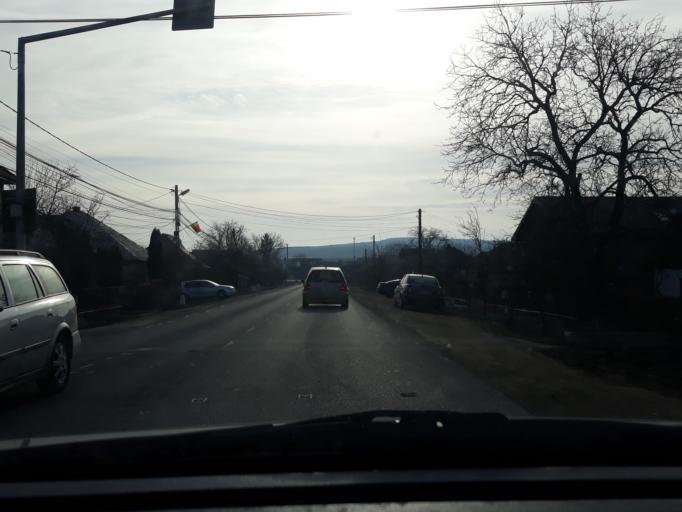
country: RO
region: Salaj
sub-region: Comuna Criseni
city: Criseni
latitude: 47.2295
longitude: 23.0417
